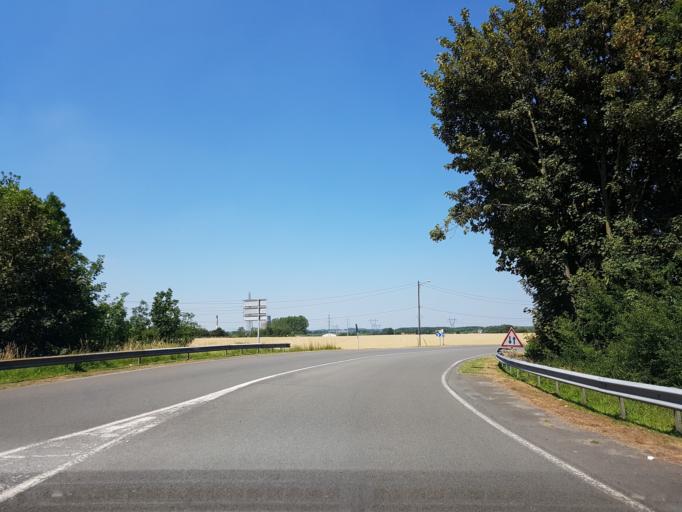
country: FR
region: Nord-Pas-de-Calais
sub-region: Departement du Nord
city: Neuville-sur-Escaut
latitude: 50.2911
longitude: 3.3573
